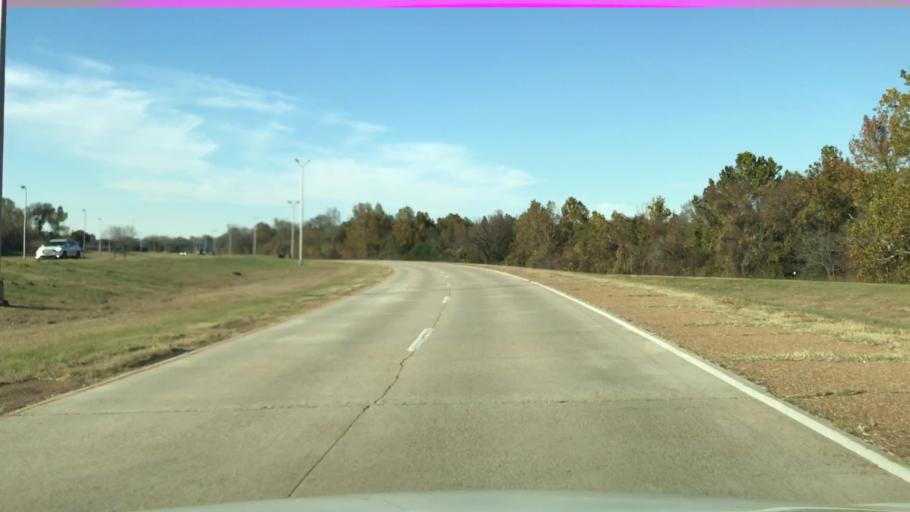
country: US
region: Louisiana
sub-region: Bossier Parish
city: Bossier City
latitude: 32.4840
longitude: -93.6937
